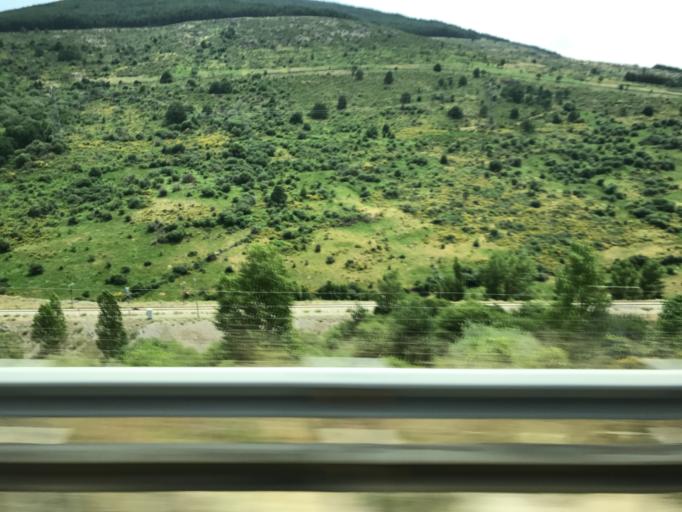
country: ES
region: Madrid
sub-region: Provincia de Madrid
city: Robregordo
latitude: 41.1117
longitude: -3.5882
